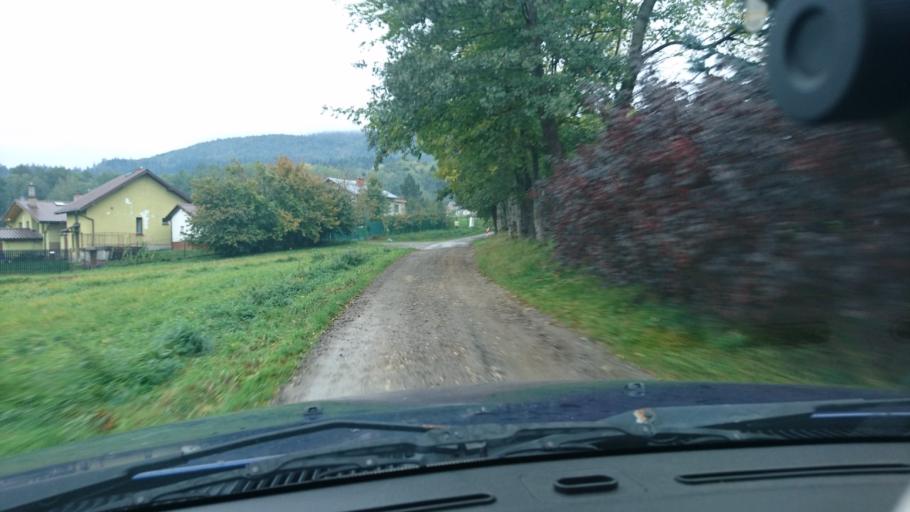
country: PL
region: Silesian Voivodeship
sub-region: Powiat bielski
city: Bujakow
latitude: 49.8450
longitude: 19.1773
